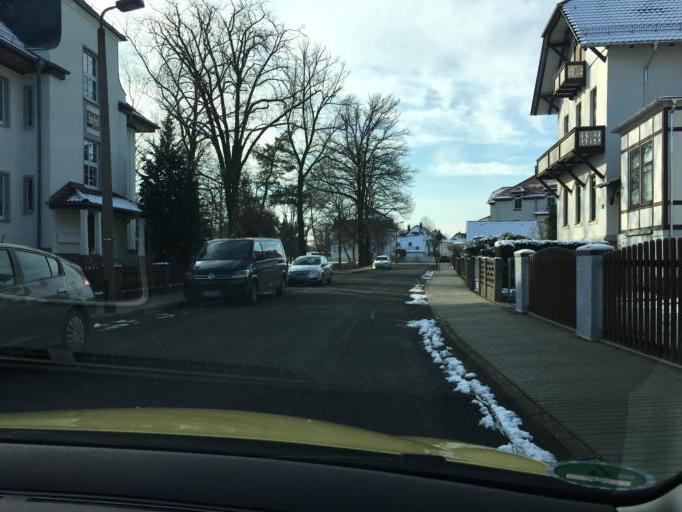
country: DE
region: Saxony
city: Bad Lausick
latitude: 51.1477
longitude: 12.6535
